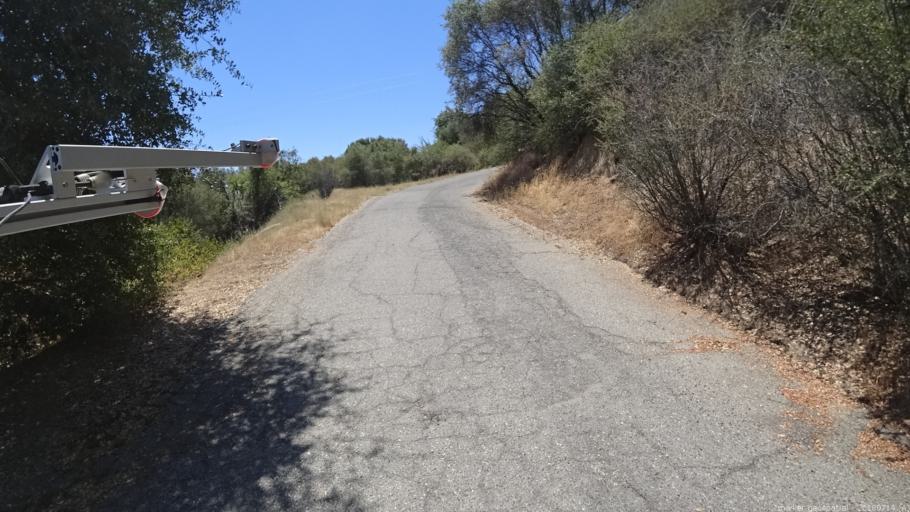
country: US
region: California
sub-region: Madera County
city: Ahwahnee
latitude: 37.3960
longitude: -119.7356
